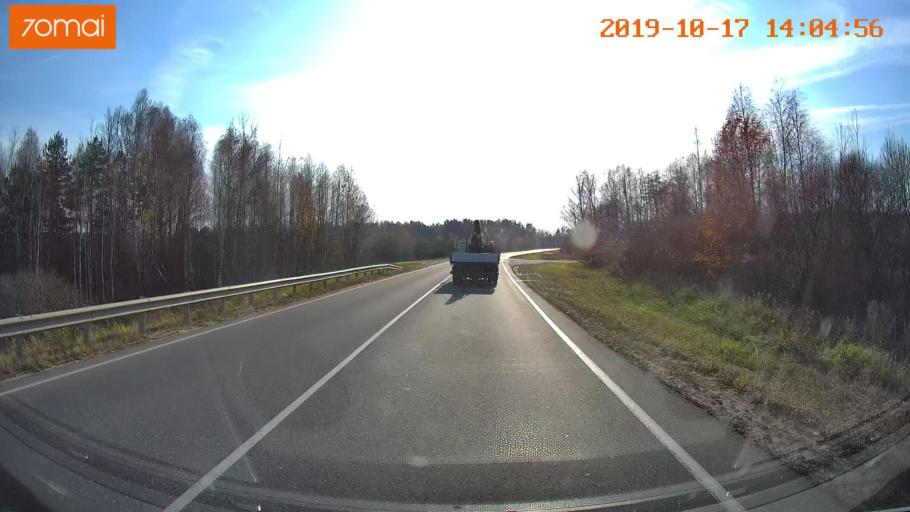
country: RU
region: Rjazan
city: Spas-Klepiki
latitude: 55.1205
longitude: 40.1330
